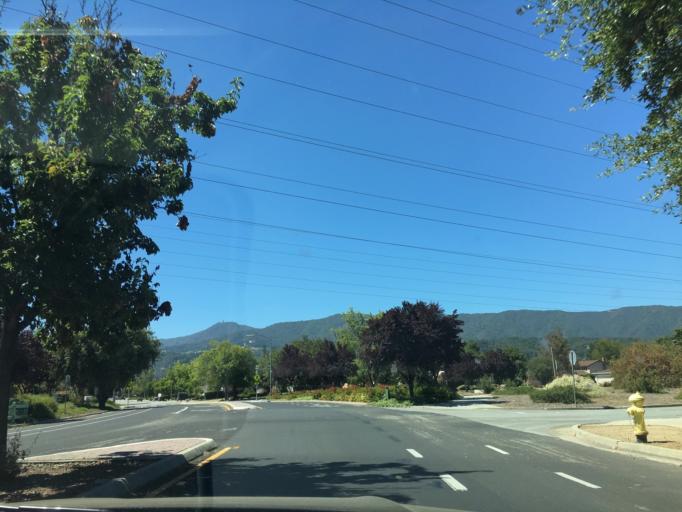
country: US
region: California
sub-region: Santa Clara County
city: Cambrian Park
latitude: 37.2331
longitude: -121.8764
